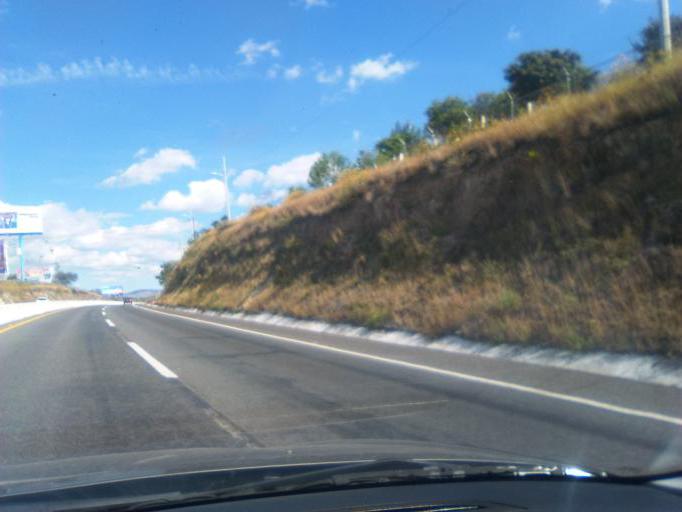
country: MX
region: Guanajuato
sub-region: Silao de la Victoria
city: Aguas Buenas
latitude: 20.9583
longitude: -101.3615
